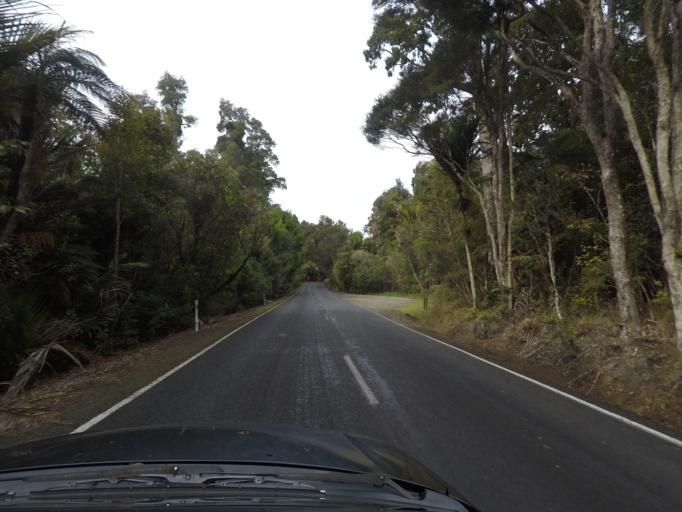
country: NZ
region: Auckland
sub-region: Auckland
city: Titirangi
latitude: -36.9431
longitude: 174.5860
